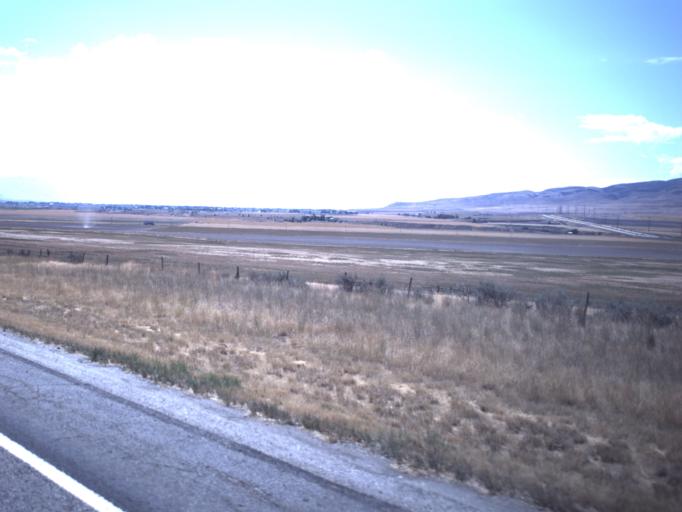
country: US
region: Utah
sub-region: Box Elder County
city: Garland
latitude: 41.8841
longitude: -112.1583
